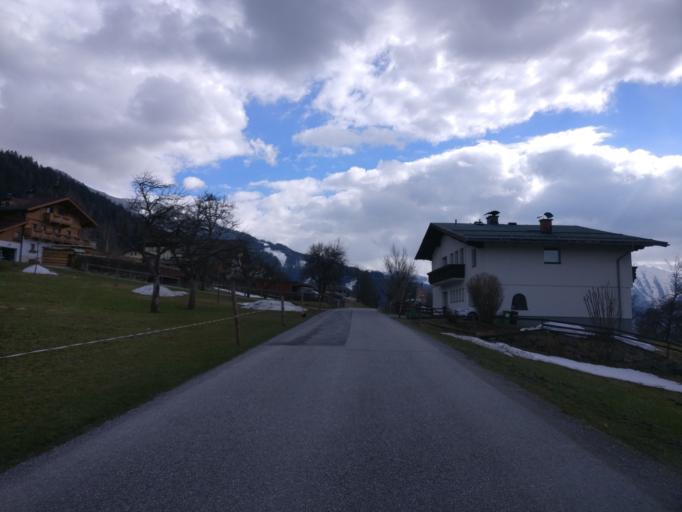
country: AT
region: Salzburg
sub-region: Politischer Bezirk Sankt Johann im Pongau
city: Bischofshofen
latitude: 47.4134
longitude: 13.2287
